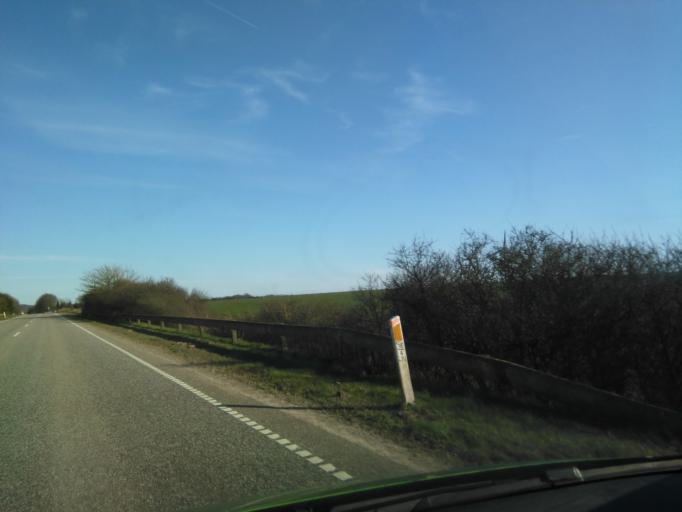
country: DK
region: Central Jutland
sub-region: Horsens Kommune
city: Braedstrup
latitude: 55.9078
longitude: 9.5900
